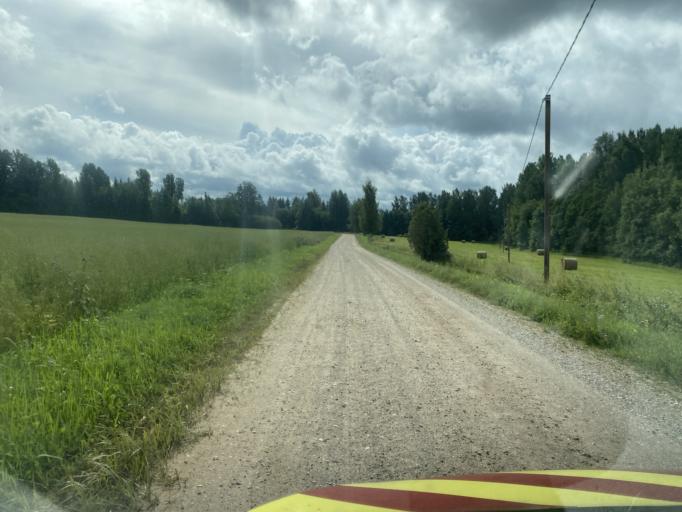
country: EE
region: Viljandimaa
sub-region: Karksi vald
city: Karksi-Nuia
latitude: 58.0624
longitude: 25.5324
